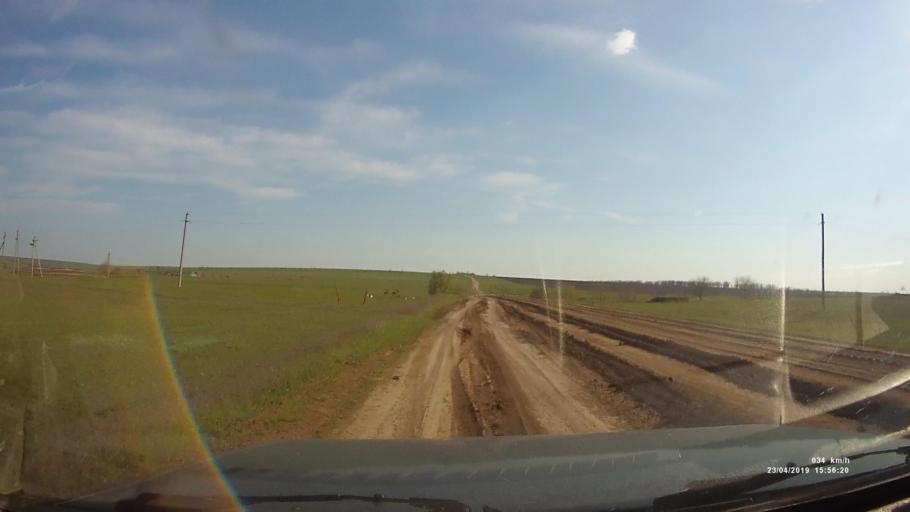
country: RU
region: Rostov
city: Remontnoye
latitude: 46.5376
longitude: 43.1113
